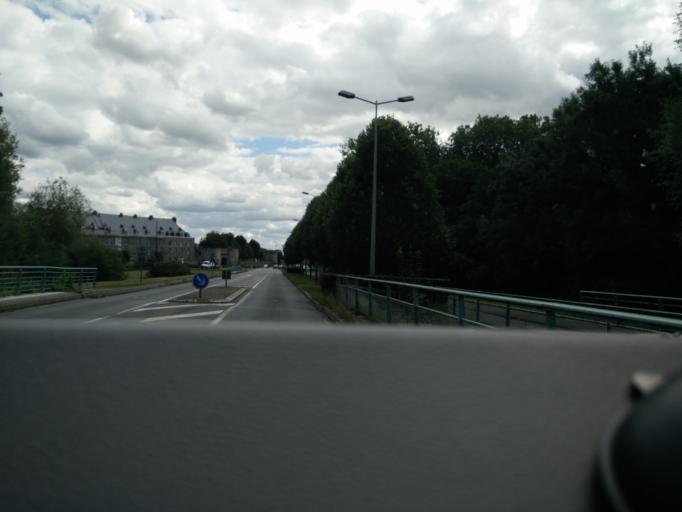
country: FR
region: Nord-Pas-de-Calais
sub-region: Departement du Nord
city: Bergues
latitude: 50.9709
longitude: 2.4245
